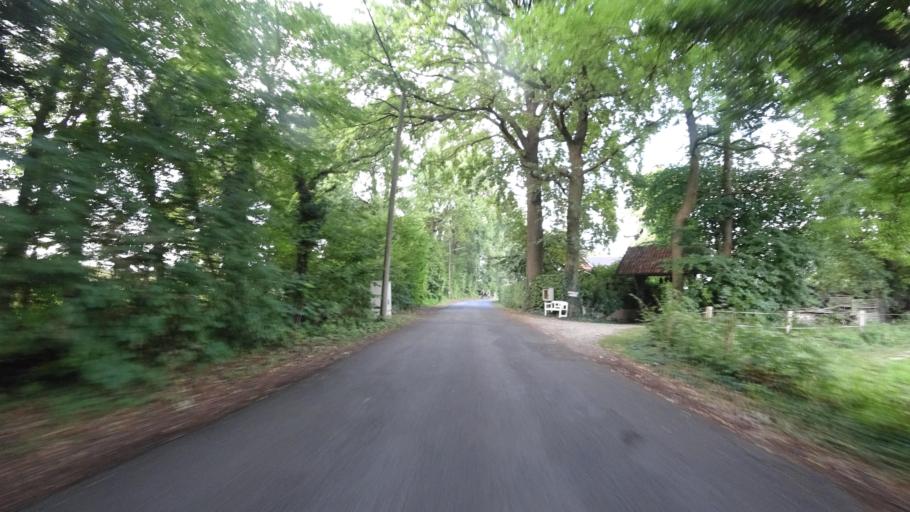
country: DE
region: North Rhine-Westphalia
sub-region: Regierungsbezirk Detmold
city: Steinhagen
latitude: 51.9480
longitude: 8.4164
